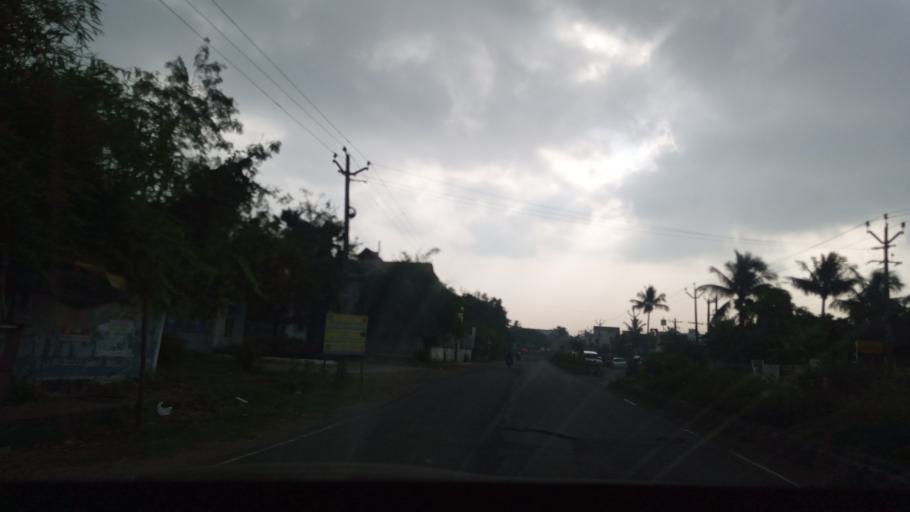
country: IN
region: Tamil Nadu
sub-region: Kancheepuram
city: Vengavasal
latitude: 12.7929
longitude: 80.2148
